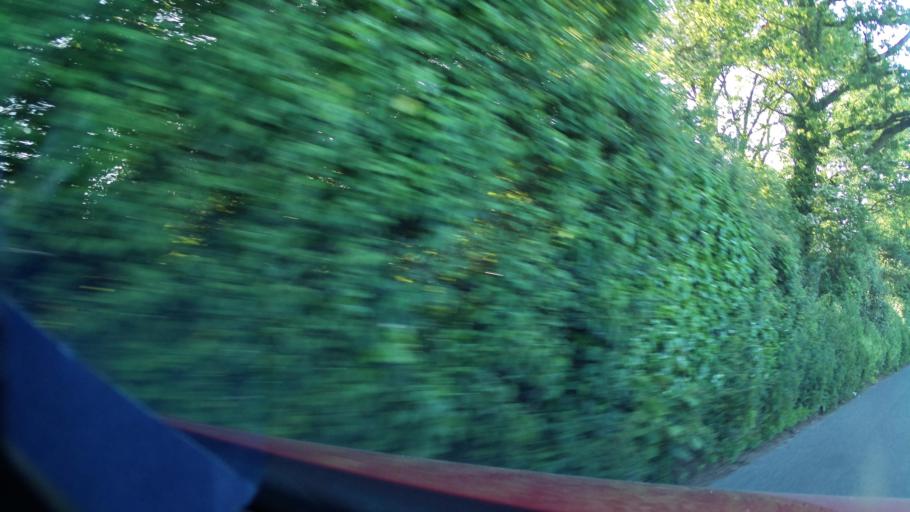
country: GB
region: England
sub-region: Devon
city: Topsham
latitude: 50.7200
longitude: -3.3919
